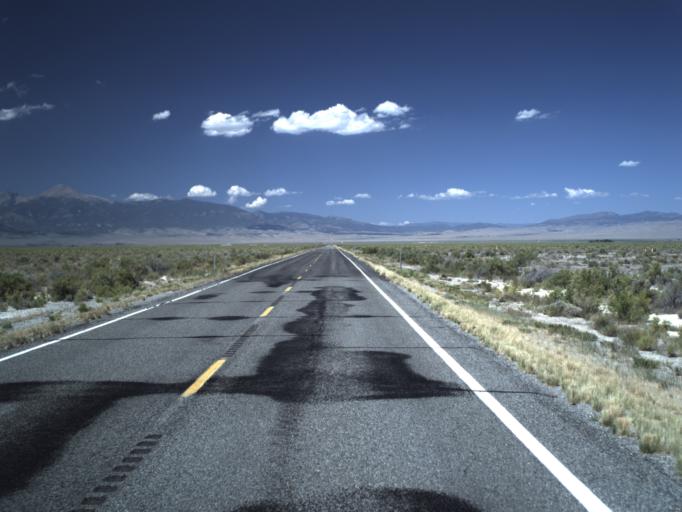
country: US
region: Nevada
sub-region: White Pine County
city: McGill
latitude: 39.0468
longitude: -113.9143
